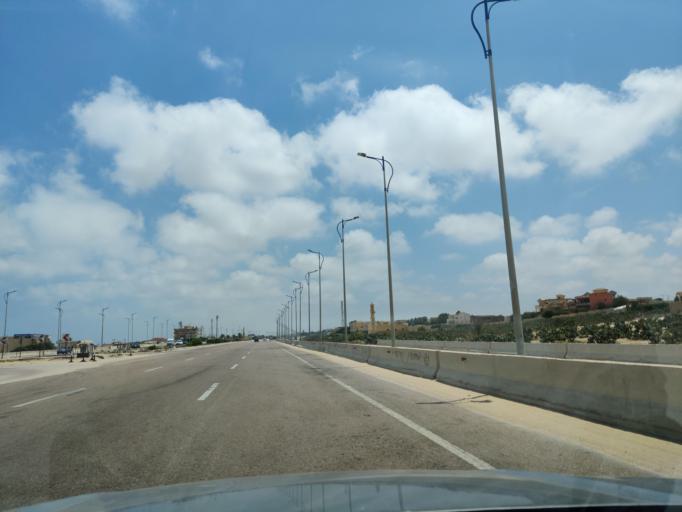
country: EG
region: Alexandria
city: Alexandria
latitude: 30.9636
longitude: 29.5497
